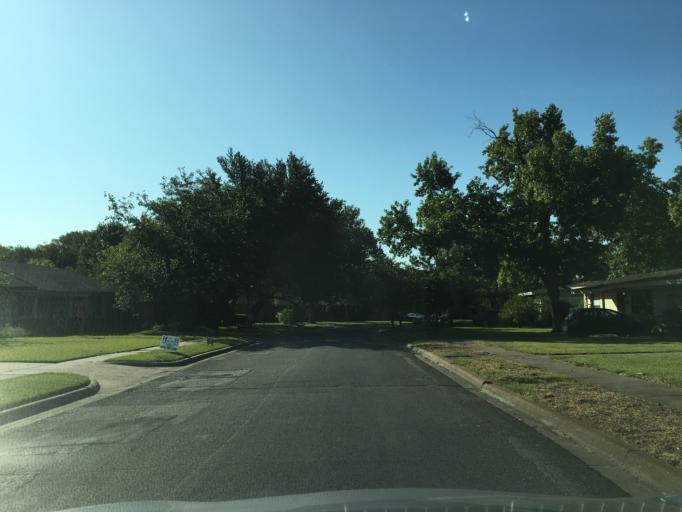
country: US
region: Texas
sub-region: Dallas County
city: Garland
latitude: 32.8580
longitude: -96.7069
